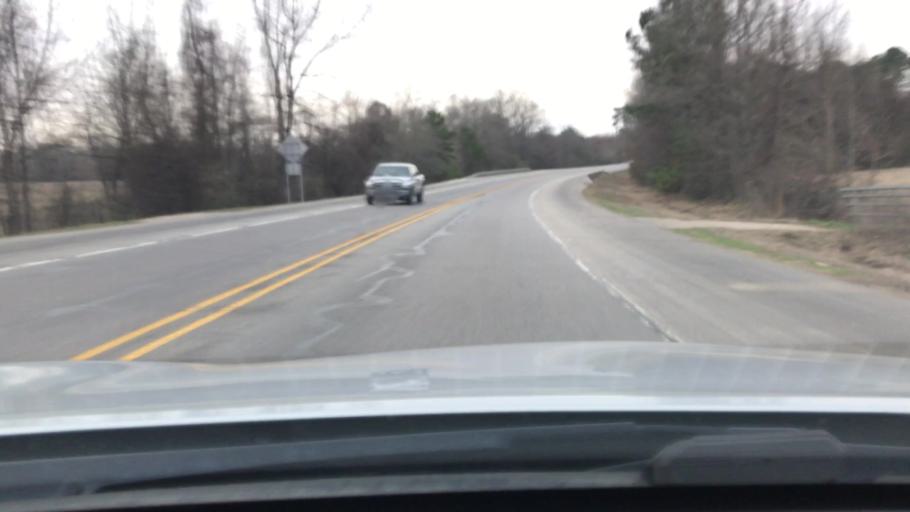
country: US
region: Arkansas
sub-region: Hempstead County
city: Hope
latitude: 33.6856
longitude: -93.5771
